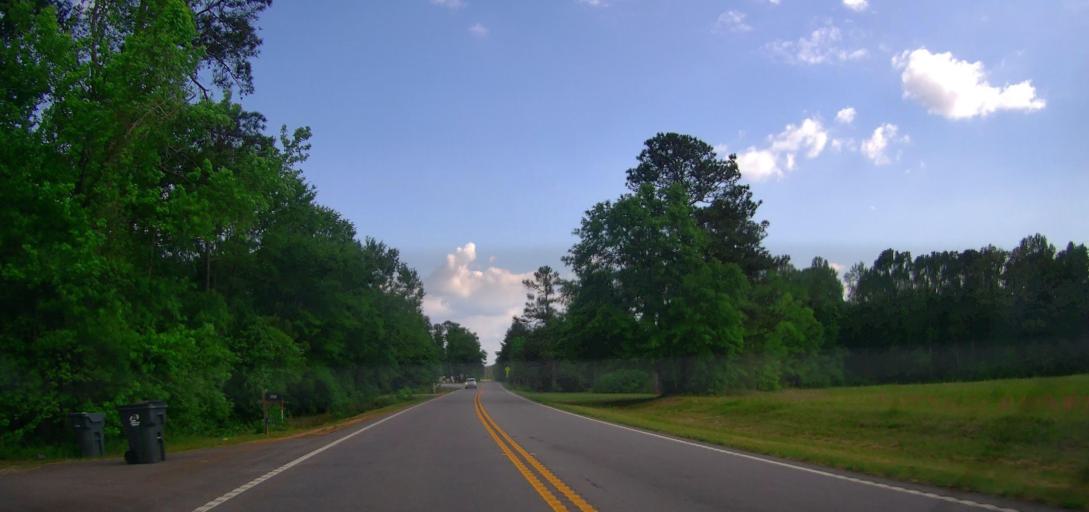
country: US
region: Georgia
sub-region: Baldwin County
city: Hardwick
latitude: 33.0550
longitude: -83.1246
